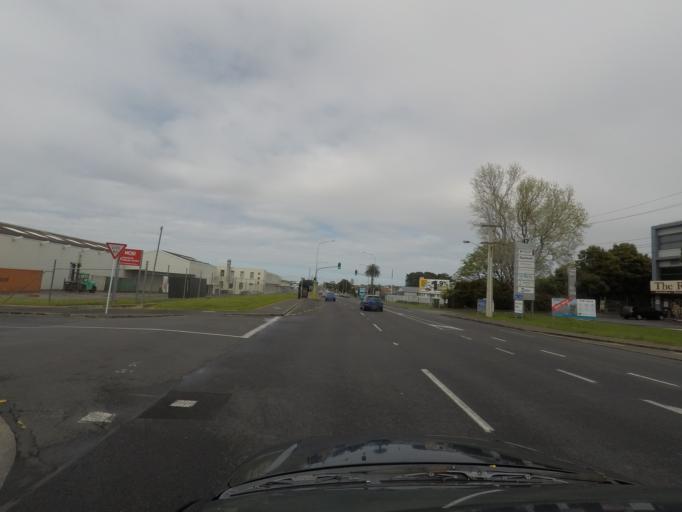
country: NZ
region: Auckland
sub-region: Auckland
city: Tamaki
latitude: -36.9005
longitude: 174.8437
